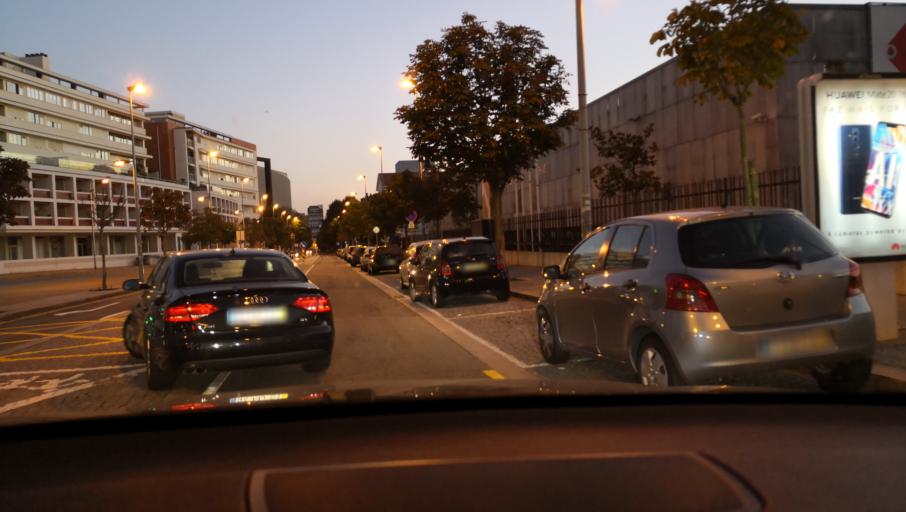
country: PT
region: Porto
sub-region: Matosinhos
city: Senhora da Hora
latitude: 41.1649
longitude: -8.6428
